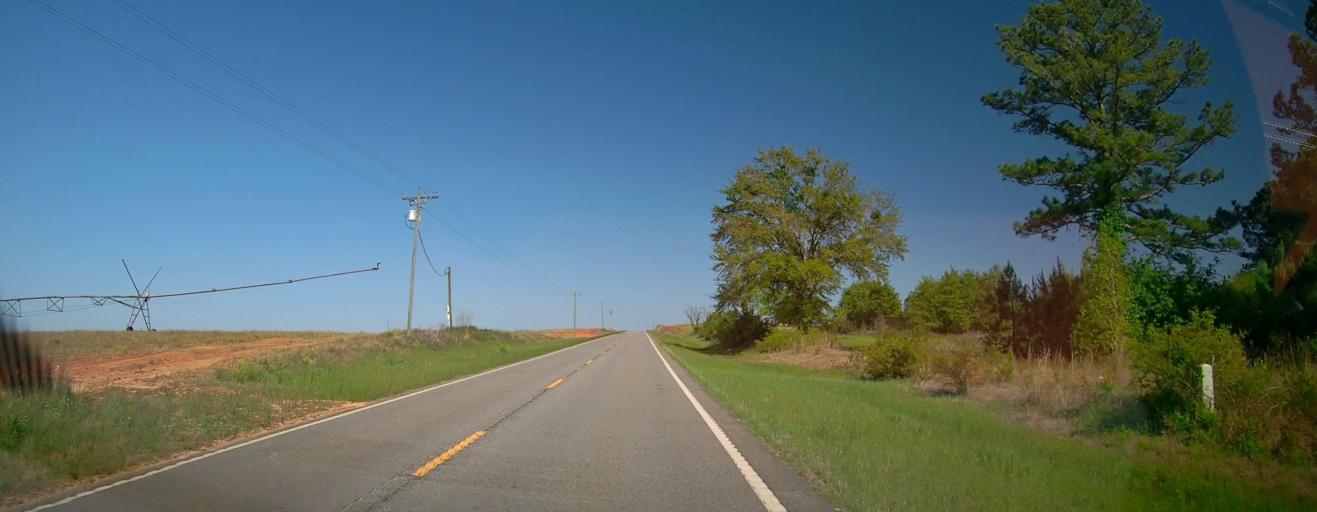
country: US
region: Georgia
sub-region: Dooly County
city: Unadilla
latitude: 32.2600
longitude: -83.6766
